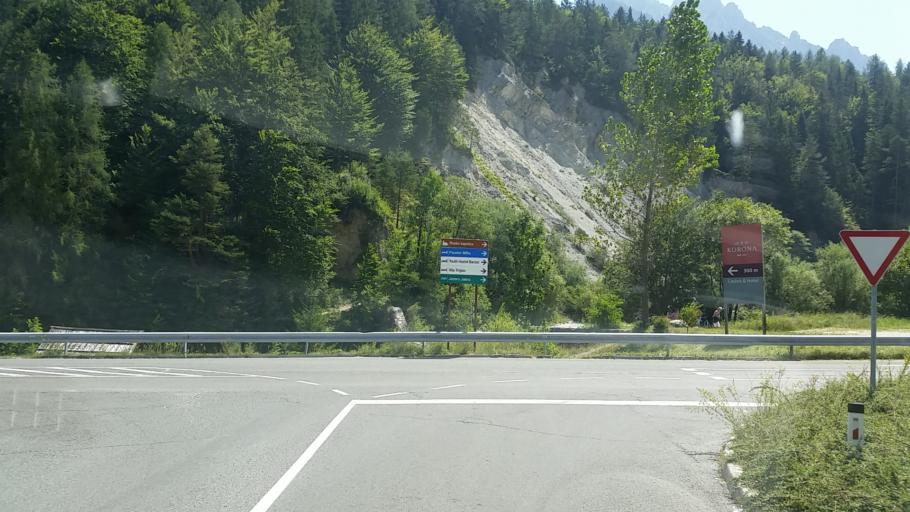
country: SI
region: Kranjska Gora
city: Kranjska Gora
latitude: 46.4817
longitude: 13.7822
